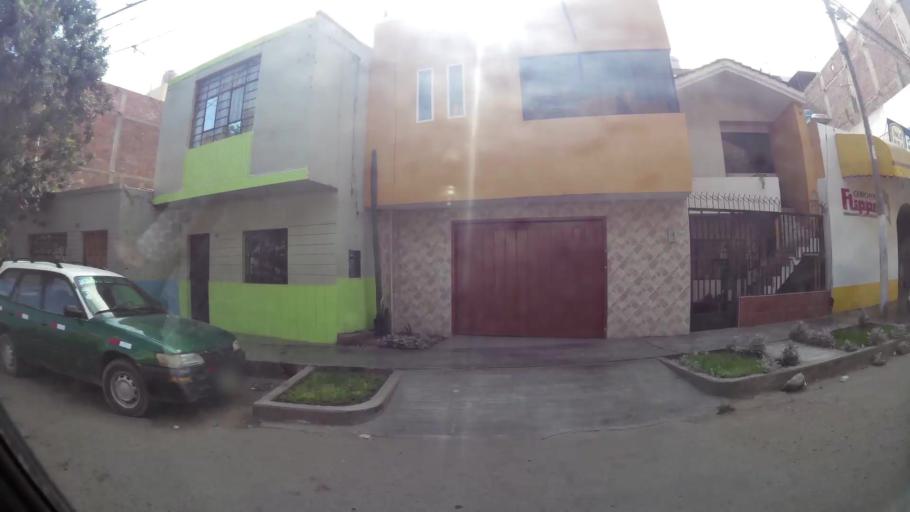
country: PE
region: La Libertad
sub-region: Provincia de Trujillo
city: Trujillo
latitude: -8.1056
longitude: -79.0128
